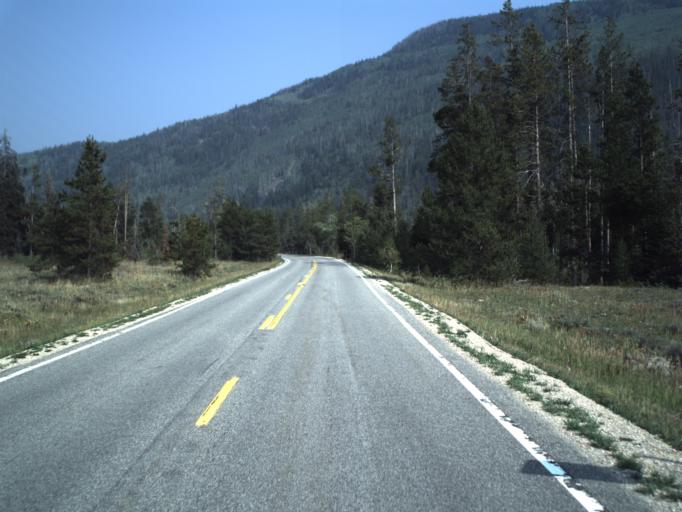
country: US
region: Utah
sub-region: Summit County
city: Francis
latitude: 40.5779
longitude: -111.0344
